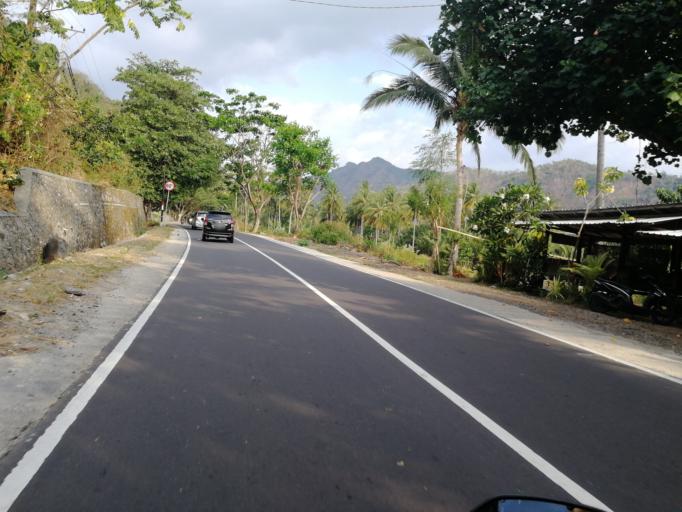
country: ID
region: West Nusa Tenggara
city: Karangsubagan
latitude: -8.4395
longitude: 116.0418
